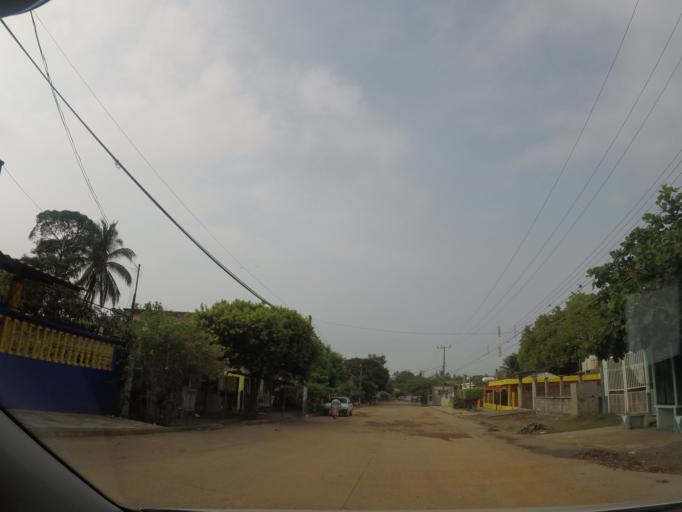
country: MX
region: Oaxaca
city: Matias Romero
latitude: 16.8784
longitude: -95.0473
